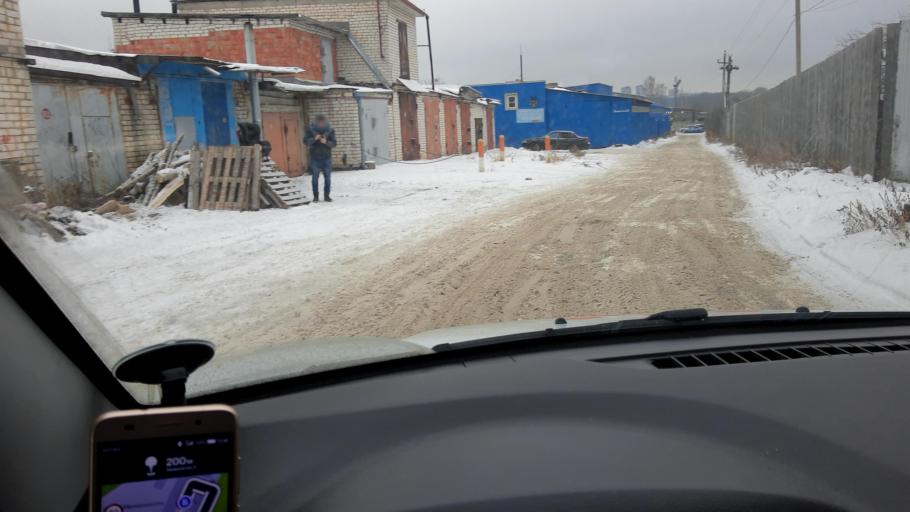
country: RU
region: Nizjnij Novgorod
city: Nizhniy Novgorod
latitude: 56.2494
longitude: 43.9590
